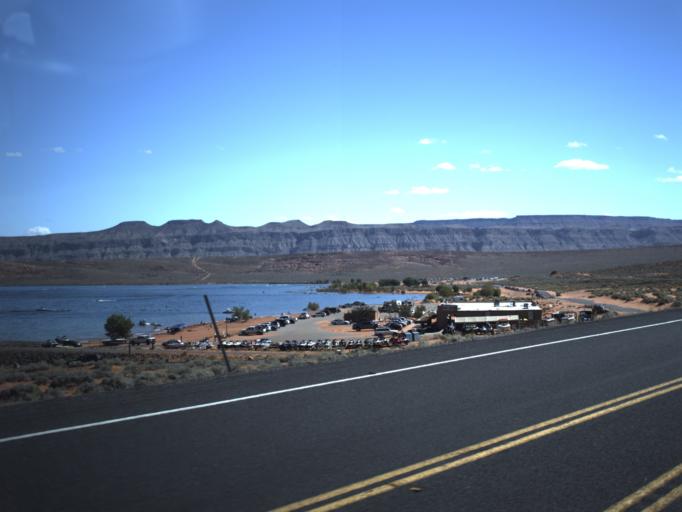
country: US
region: Utah
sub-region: Washington County
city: Washington
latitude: 37.1062
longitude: -113.3958
